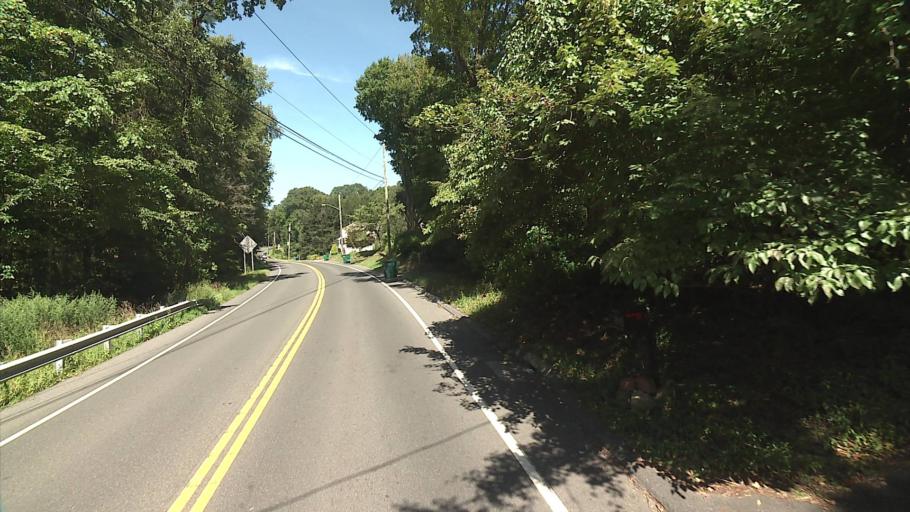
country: US
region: Connecticut
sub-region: New Haven County
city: Ansonia
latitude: 41.3686
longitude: -73.1354
